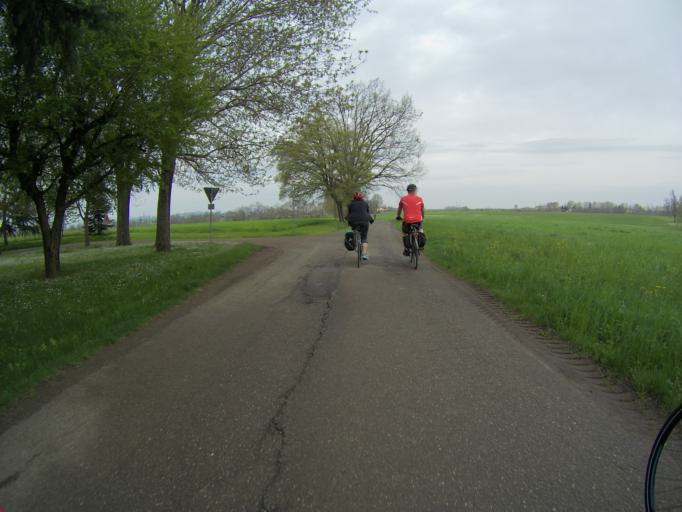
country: IT
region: Emilia-Romagna
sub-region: Provincia di Reggio Emilia
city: San Bartolomeo
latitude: 44.6657
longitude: 10.5576
